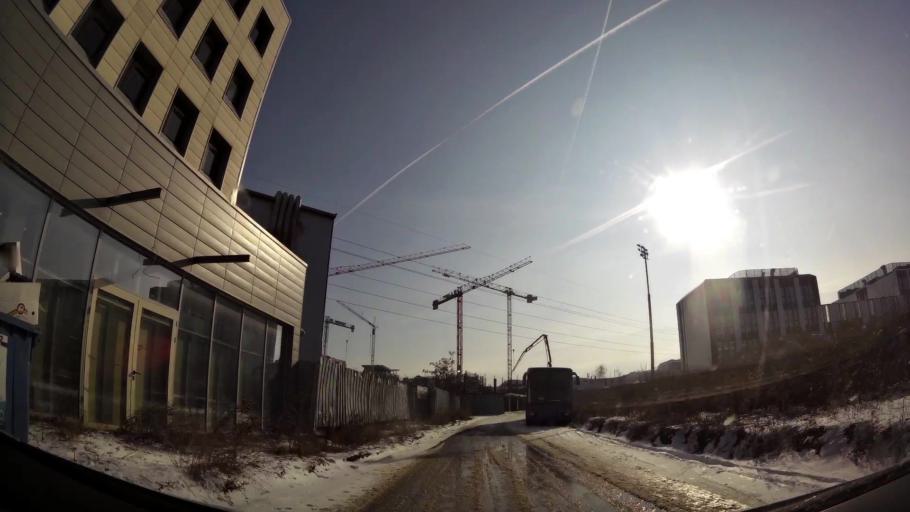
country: BG
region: Sofia-Capital
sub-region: Stolichna Obshtina
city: Sofia
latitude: 42.6565
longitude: 23.3189
